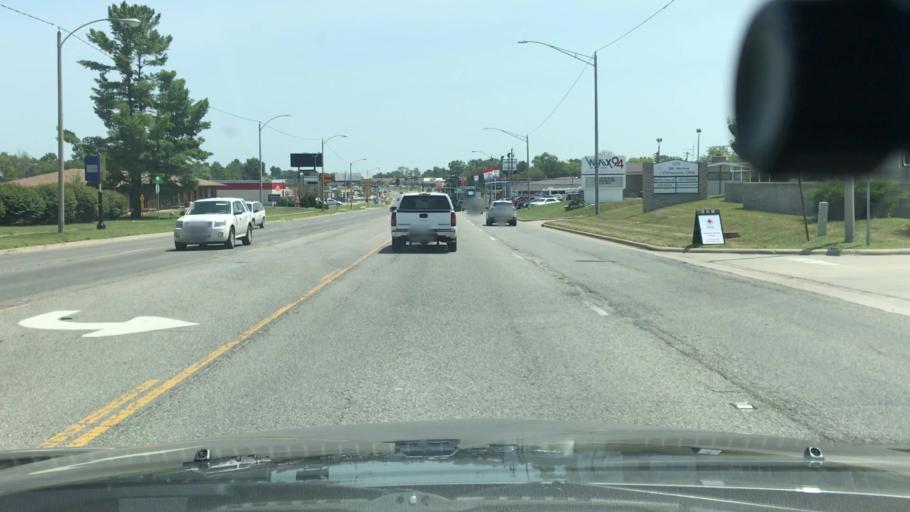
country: US
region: Illinois
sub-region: Jefferson County
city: Mount Vernon
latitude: 38.3143
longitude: -88.9370
